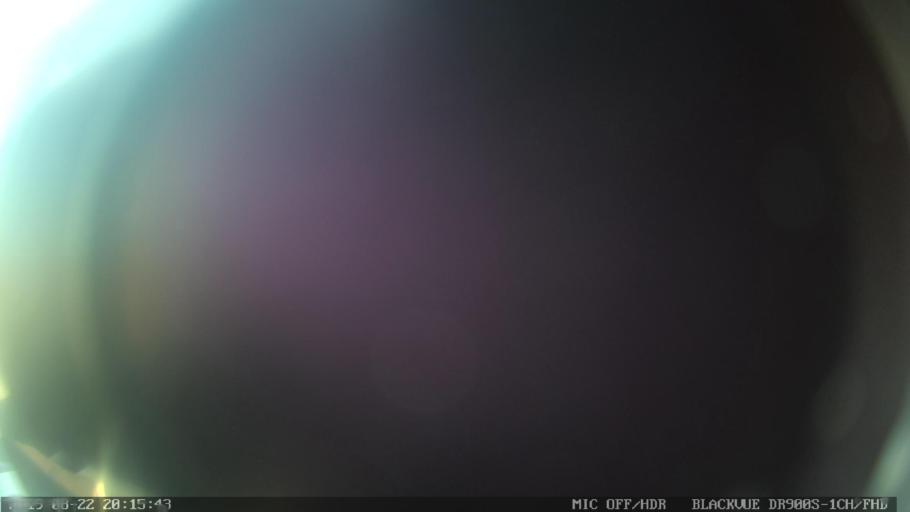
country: PT
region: Guarda
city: Alcains
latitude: 39.9226
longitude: -7.4443
